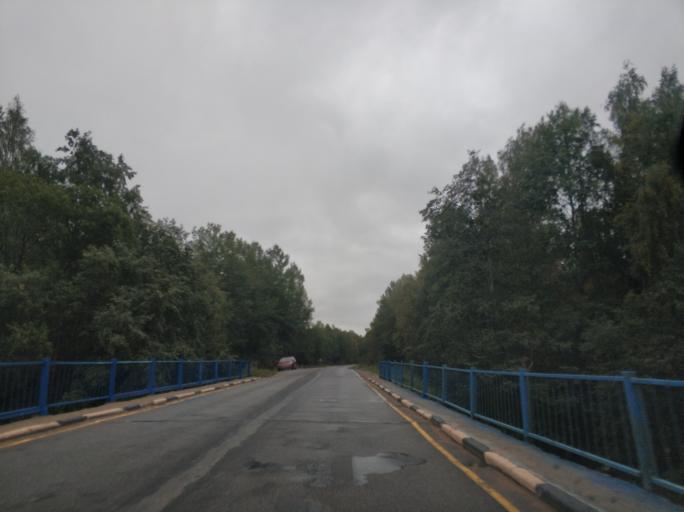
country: RU
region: Leningrad
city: Borisova Griva
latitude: 60.1351
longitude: 30.9595
